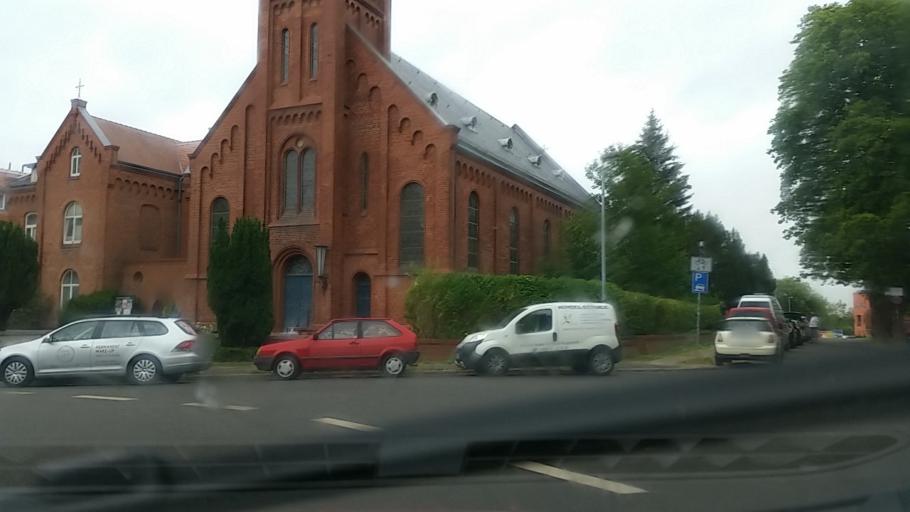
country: DE
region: Mecklenburg-Vorpommern
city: Wismar
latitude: 53.8877
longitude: 11.4705
